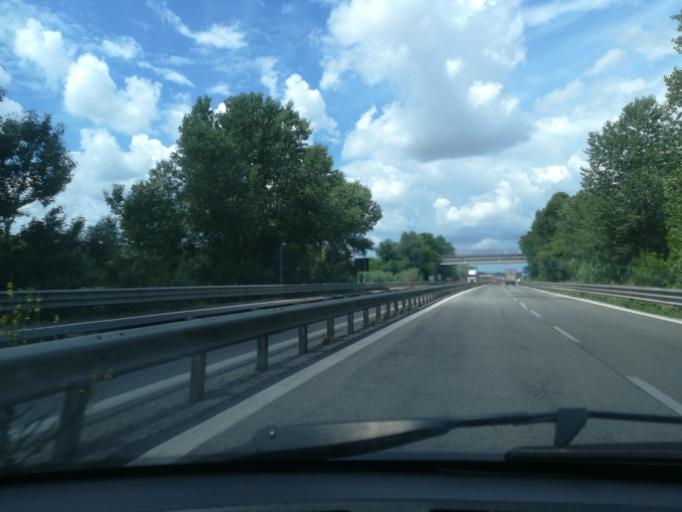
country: IT
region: The Marches
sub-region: Provincia di Macerata
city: Villa San Filippo
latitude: 43.2627
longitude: 13.5695
